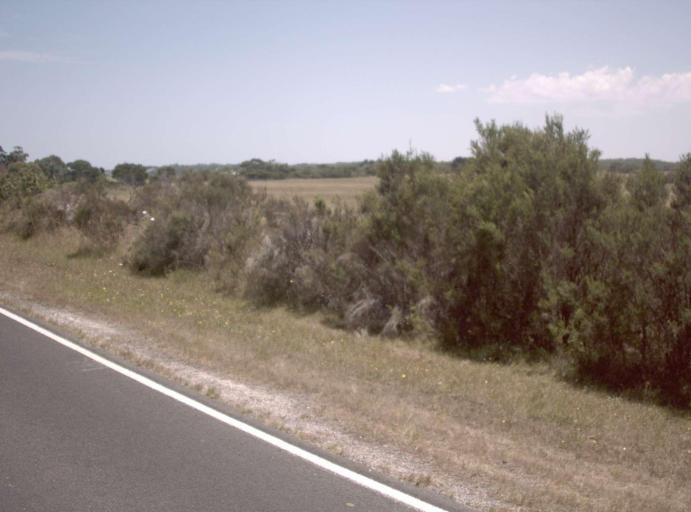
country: AU
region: Victoria
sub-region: Bass Coast
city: North Wonthaggi
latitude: -38.6836
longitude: 145.8843
